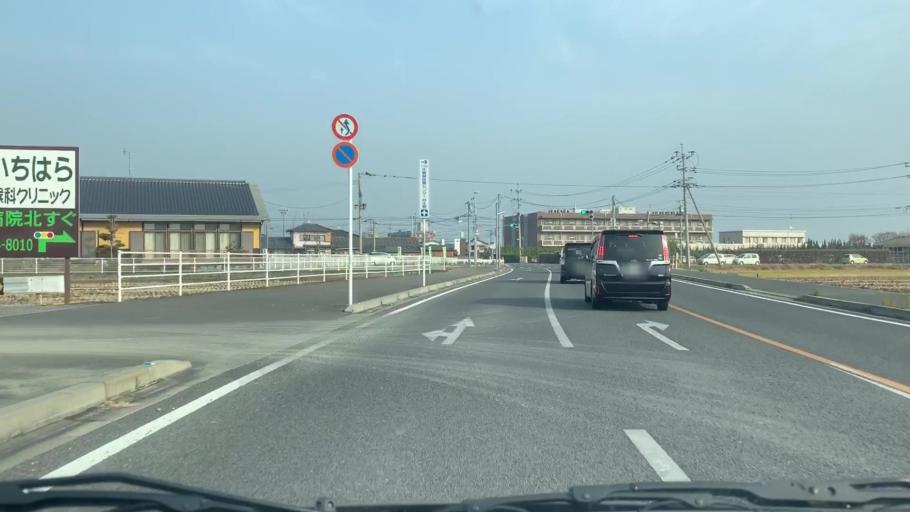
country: JP
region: Saga Prefecture
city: Saga-shi
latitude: 33.2374
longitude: 130.2581
